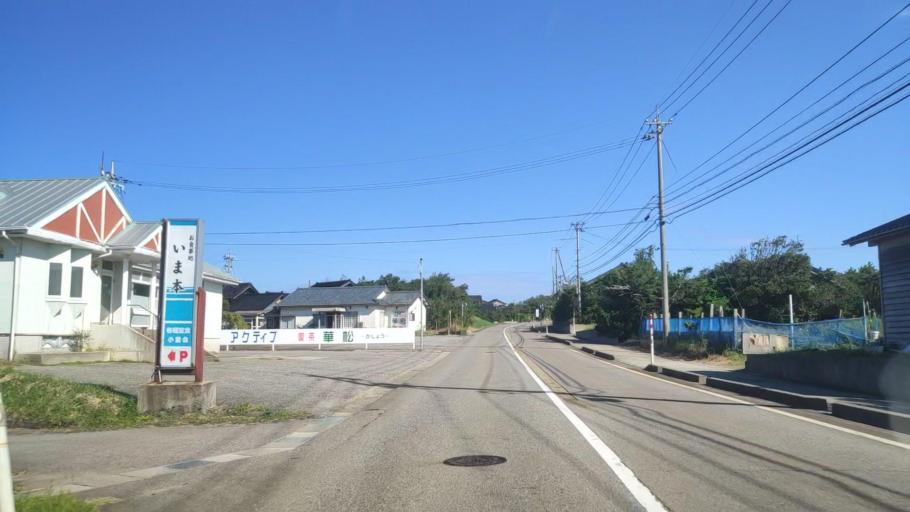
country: JP
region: Ishikawa
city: Hakui
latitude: 36.9843
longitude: 136.7759
